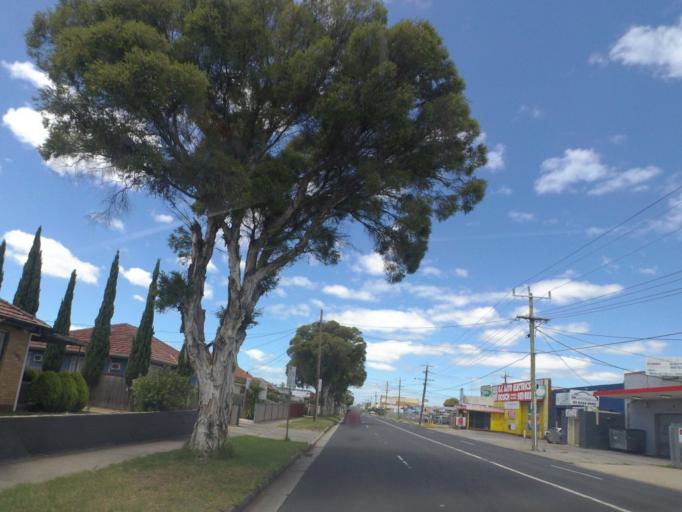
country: AU
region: Victoria
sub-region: Brimbank
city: Albion
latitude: -37.7668
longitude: 144.8307
